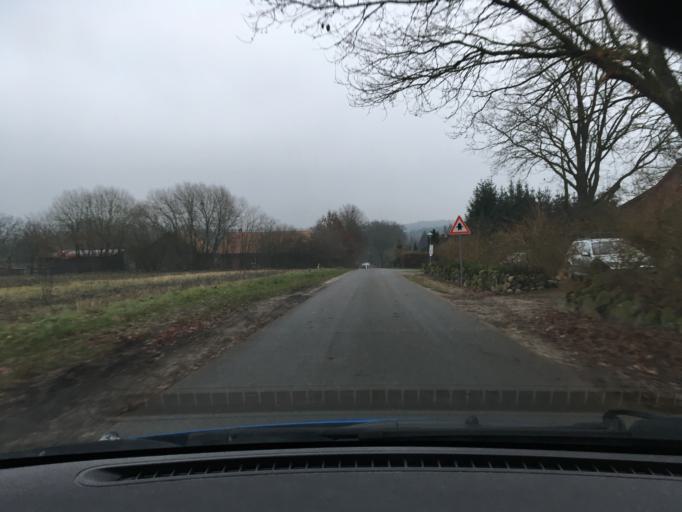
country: DE
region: Lower Saxony
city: Rehlingen
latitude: 53.1068
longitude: 10.2150
